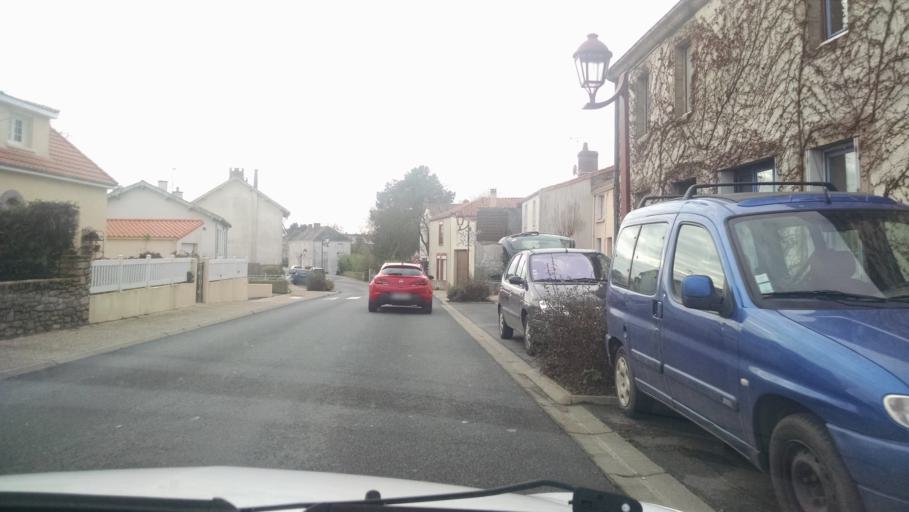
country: FR
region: Pays de la Loire
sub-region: Departement de la Loire-Atlantique
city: Saint-Hilaire-de-Clisson
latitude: 47.0625
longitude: -1.3091
